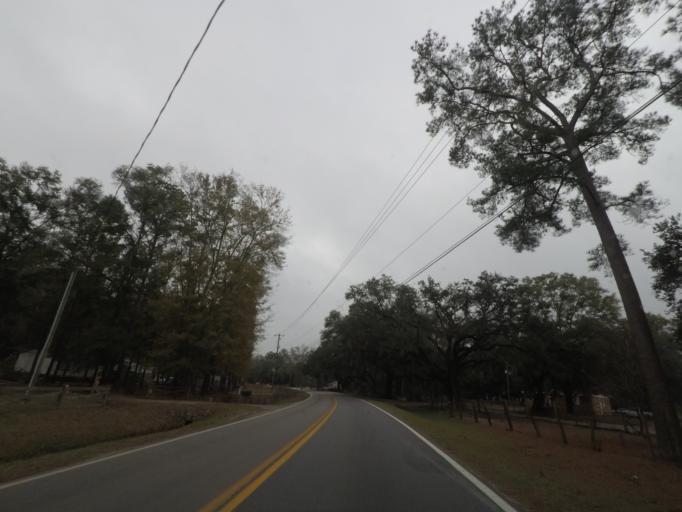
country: US
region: South Carolina
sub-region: Charleston County
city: Ravenel
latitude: 32.7239
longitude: -80.3528
